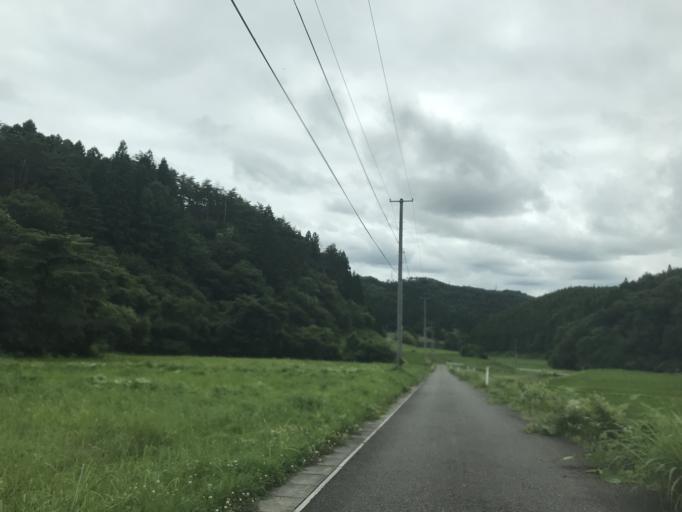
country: JP
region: Iwate
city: Ichinoseki
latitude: 38.8972
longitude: 140.9762
